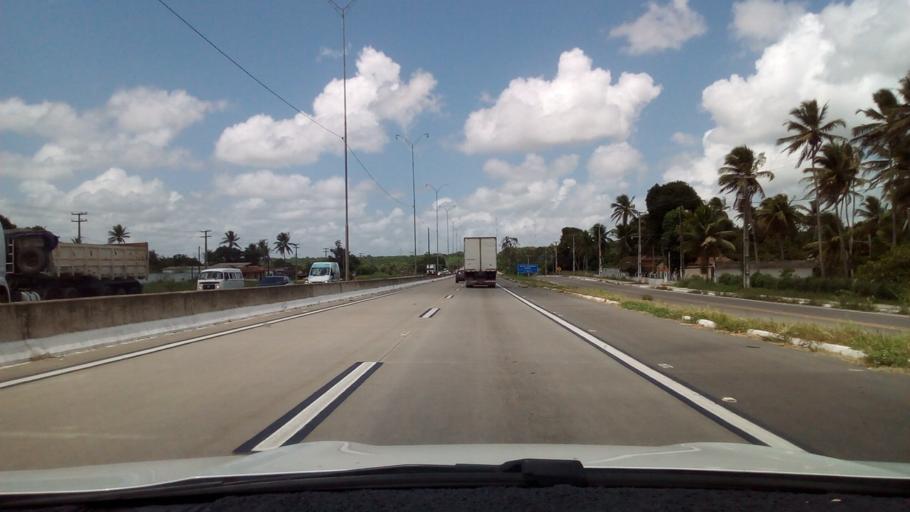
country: BR
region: Paraiba
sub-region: Conde
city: Conde
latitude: -7.3399
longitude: -34.9476
